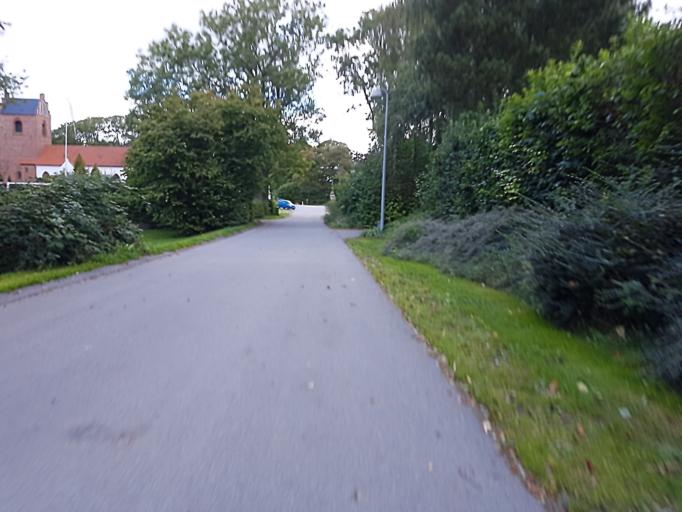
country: DK
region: Zealand
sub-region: Roskilde Kommune
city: Gundsomagle
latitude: 55.7206
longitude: 12.1597
